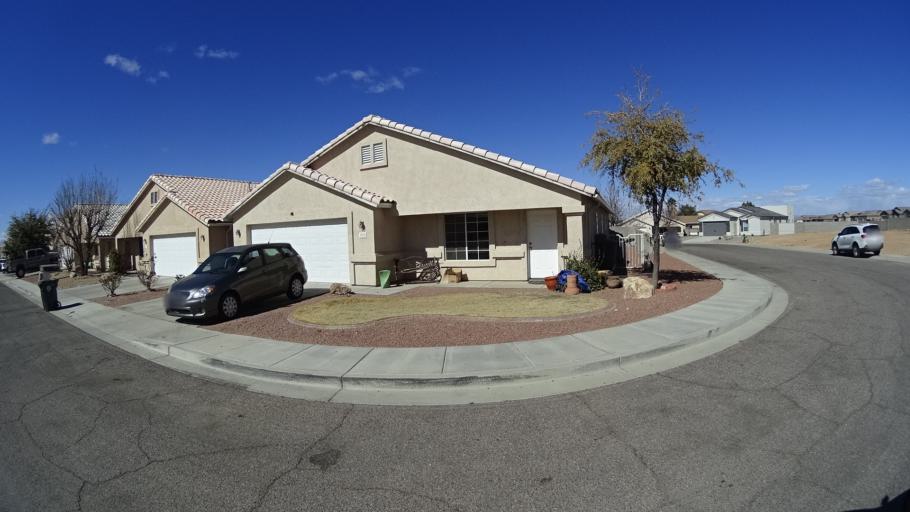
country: US
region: Arizona
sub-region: Mohave County
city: Kingman
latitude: 35.1889
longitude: -114.0076
